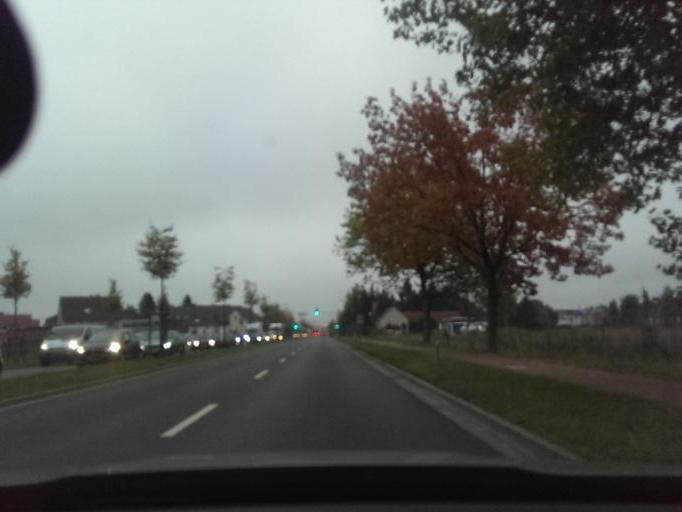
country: DE
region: Lower Saxony
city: Garbsen-Mitte
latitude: 52.4336
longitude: 9.6046
